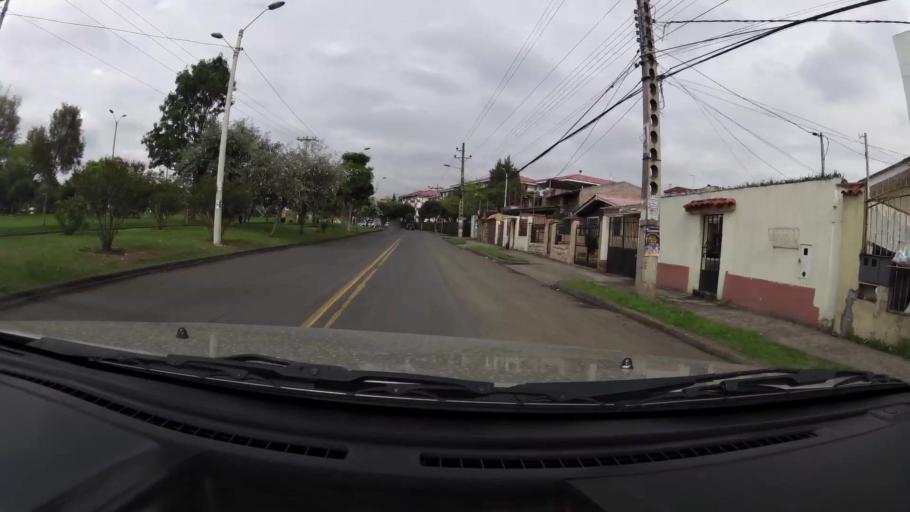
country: EC
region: Azuay
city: Cuenca
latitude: -2.9078
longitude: -78.9887
